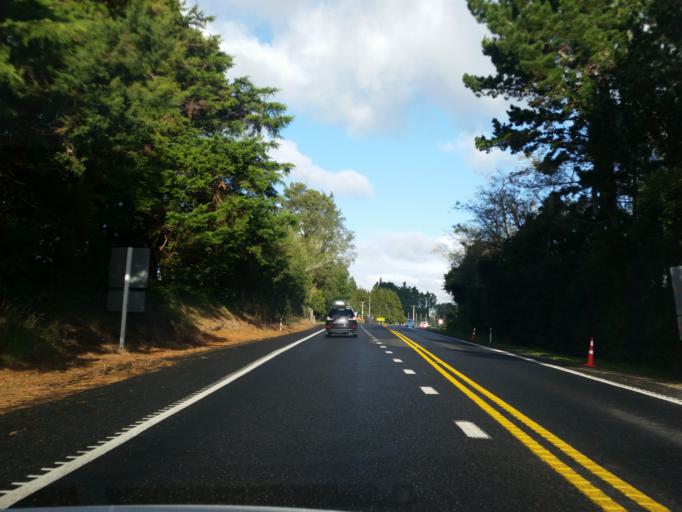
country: NZ
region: Bay of Plenty
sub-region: Western Bay of Plenty District
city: Katikati
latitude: -37.6148
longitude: 175.9491
